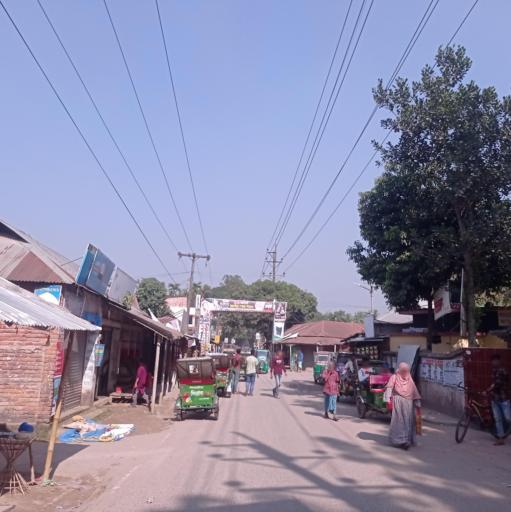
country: BD
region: Dhaka
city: Narsingdi
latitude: 24.0467
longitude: 90.6805
